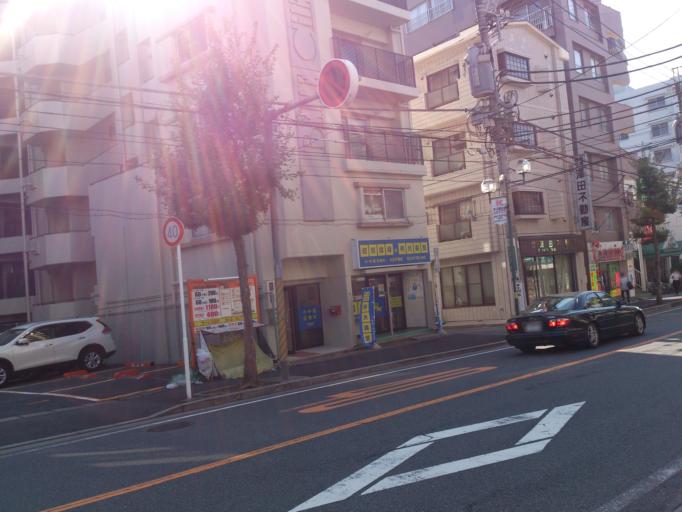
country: JP
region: Chiba
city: Matsudo
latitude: 35.7994
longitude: 139.9140
